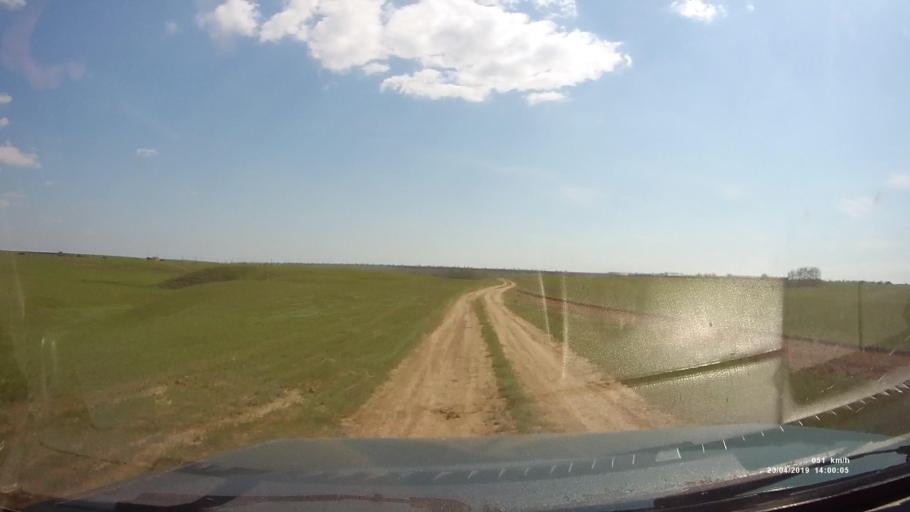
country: RU
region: Rostov
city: Remontnoye
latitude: 46.5620
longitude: 42.9469
